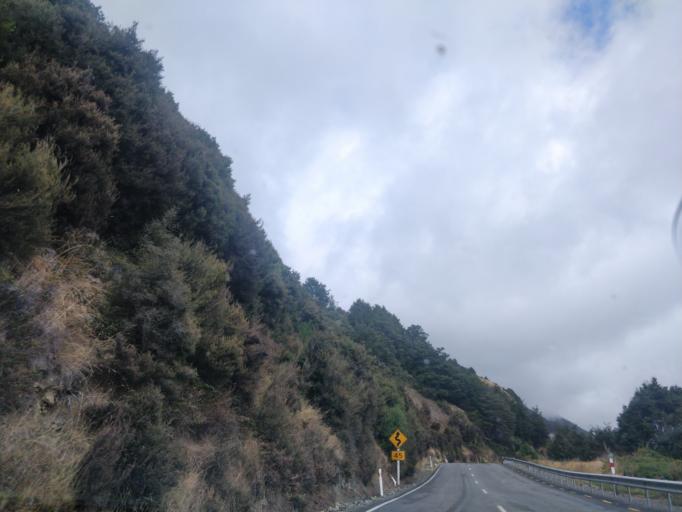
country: NZ
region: Canterbury
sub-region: Waimakariri District
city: Oxford
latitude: -43.0189
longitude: 171.7053
